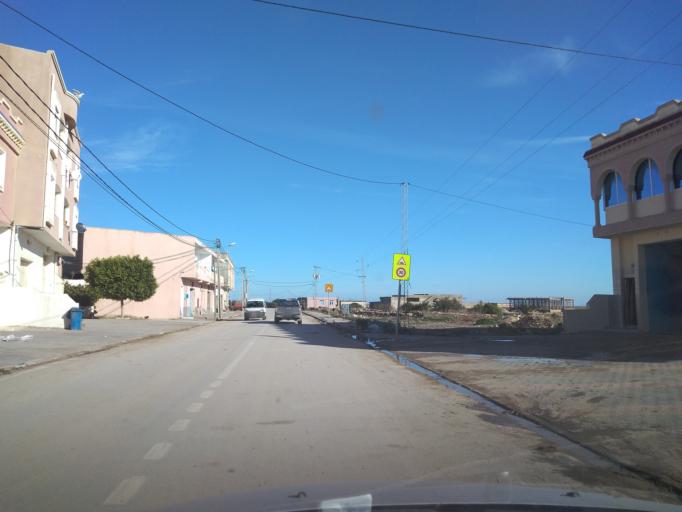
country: TN
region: Ariana
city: Qal'at al Andalus
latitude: 37.0607
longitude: 10.1303
